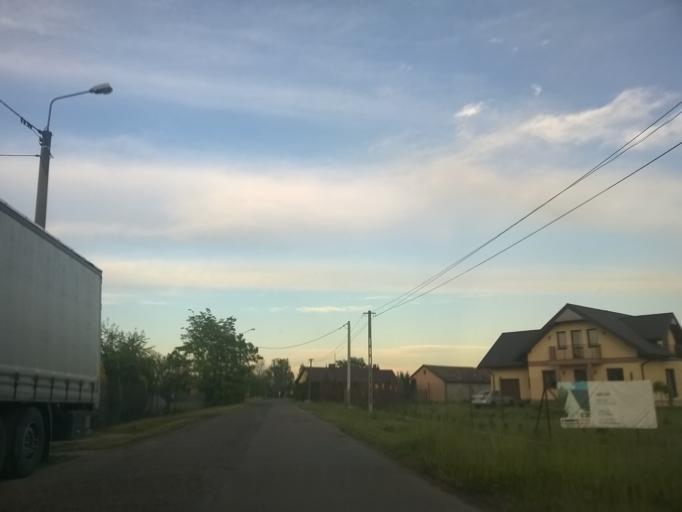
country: PL
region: Masovian Voivodeship
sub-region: Powiat piaseczynski
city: Baniocha
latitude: 52.0007
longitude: 21.1013
